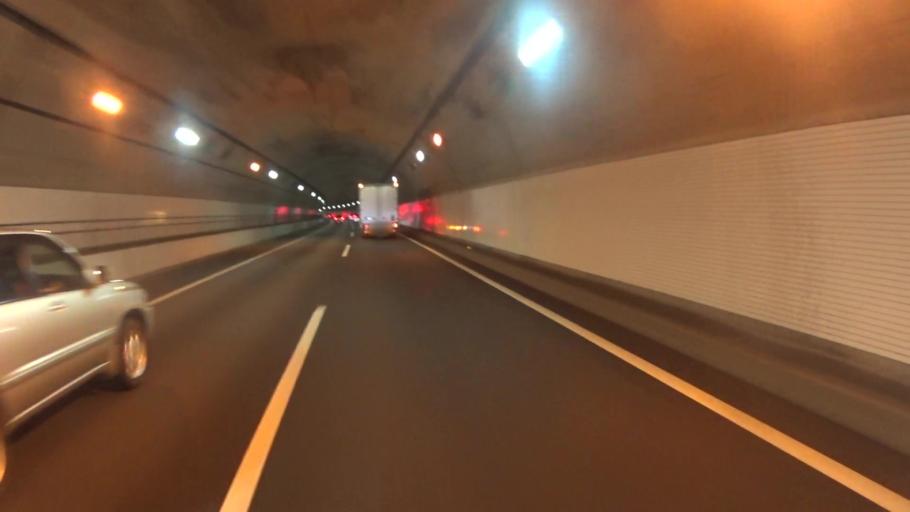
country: JP
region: Mie
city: Kameyama
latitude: 34.9151
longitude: 136.4248
